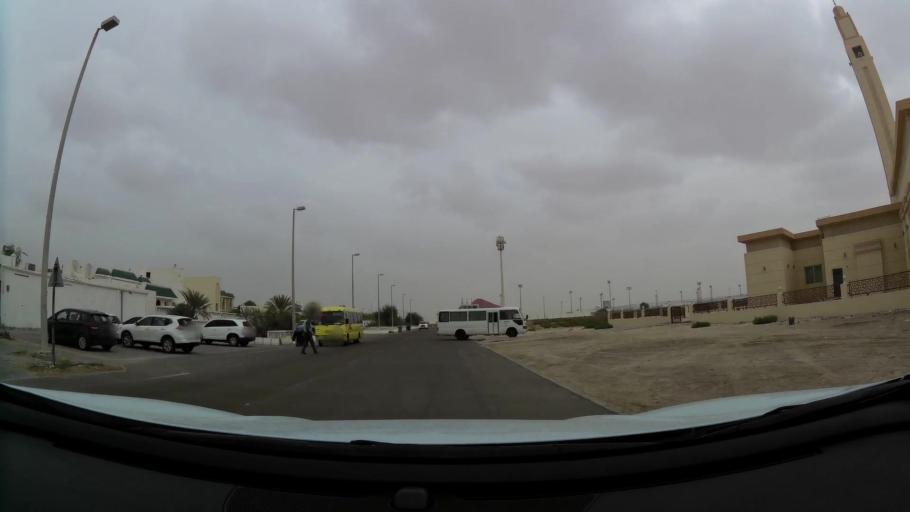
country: AE
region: Abu Dhabi
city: Abu Dhabi
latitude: 24.3784
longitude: 54.6628
